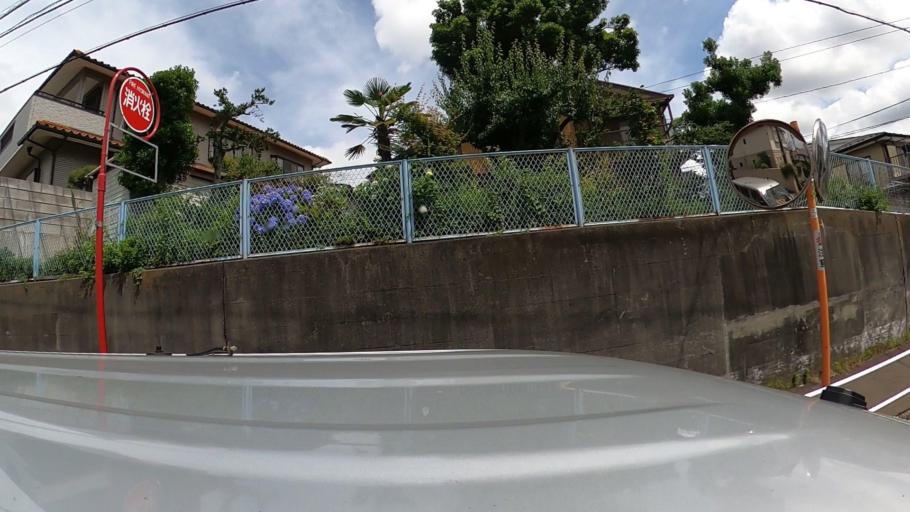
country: JP
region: Kanagawa
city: Minami-rinkan
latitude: 35.4165
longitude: 139.4730
